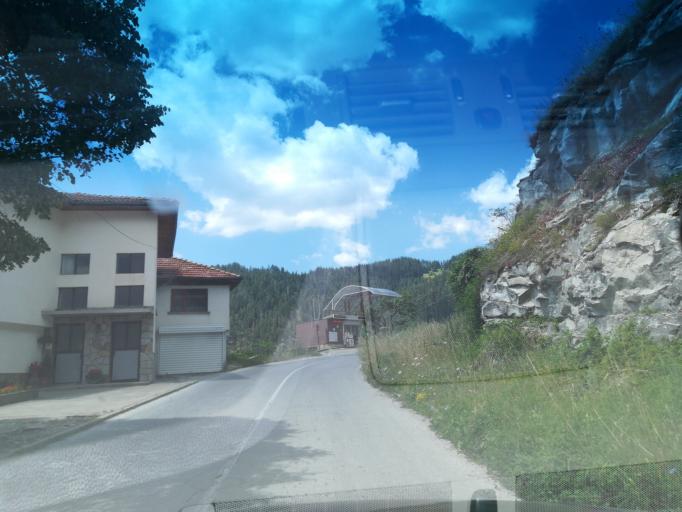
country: BG
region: Smolyan
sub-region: Obshtina Chepelare
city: Chepelare
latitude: 41.6653
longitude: 24.7756
